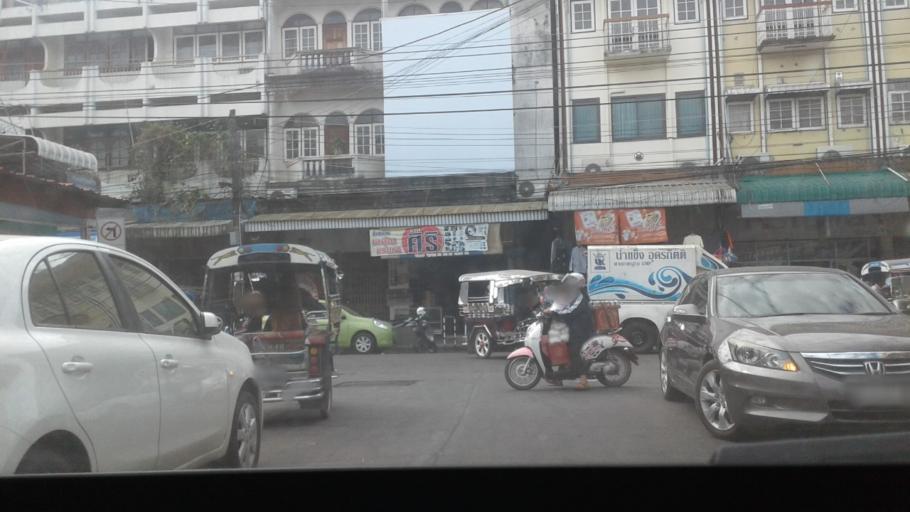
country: TH
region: Changwat Udon Thani
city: Udon Thani
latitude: 17.4079
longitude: 102.7851
